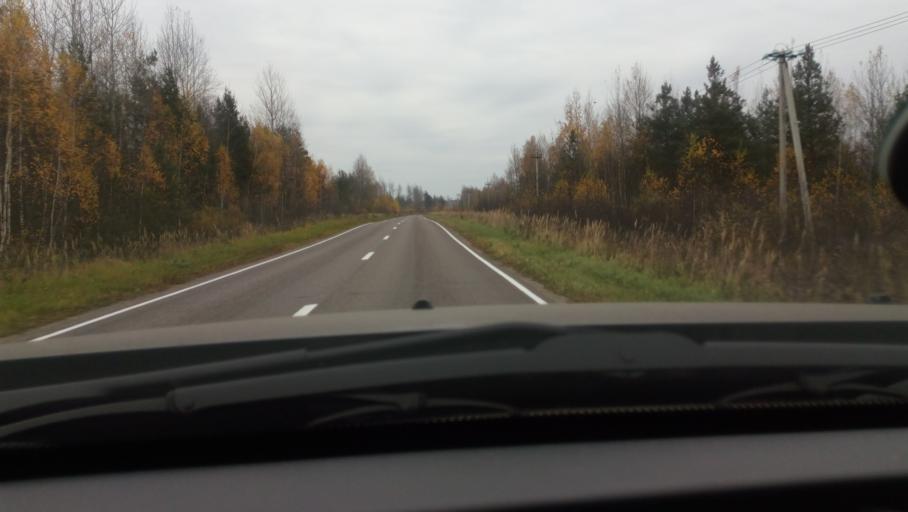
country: RU
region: Moskovskaya
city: Avsyunino
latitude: 55.5937
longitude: 39.2514
